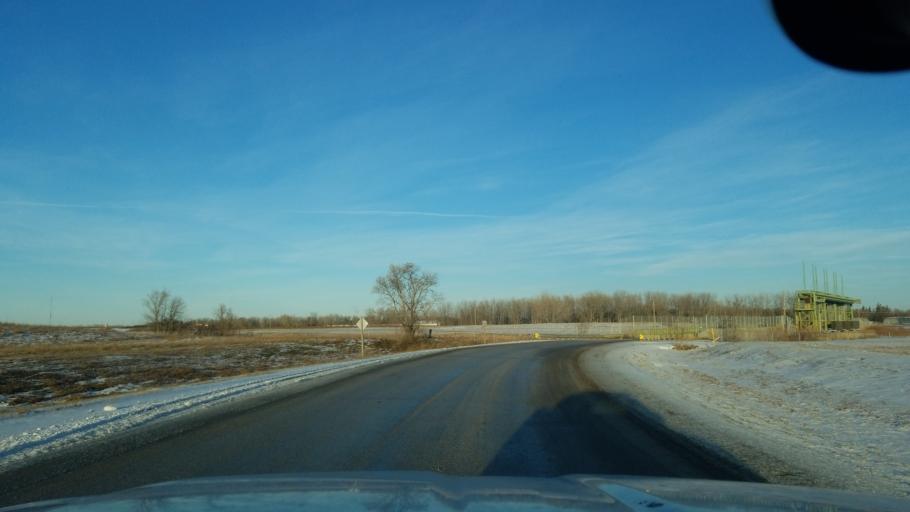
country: CA
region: Manitoba
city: Portage la Prairie
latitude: 49.9485
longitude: -98.3386
